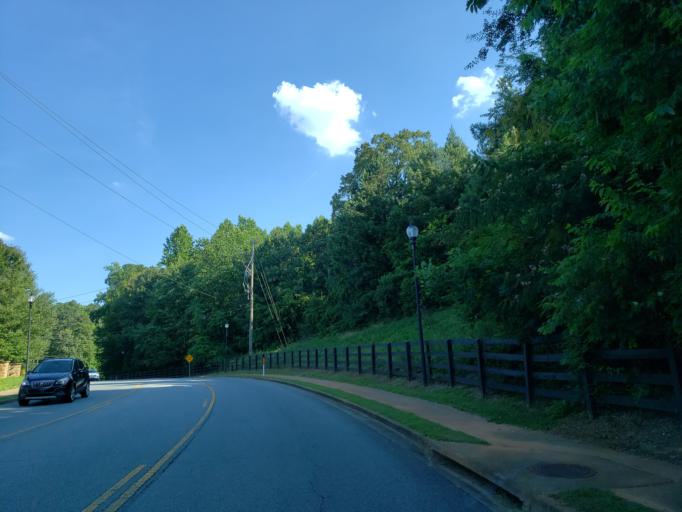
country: US
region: Georgia
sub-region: Cherokee County
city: Woodstock
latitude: 34.0986
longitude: -84.5364
